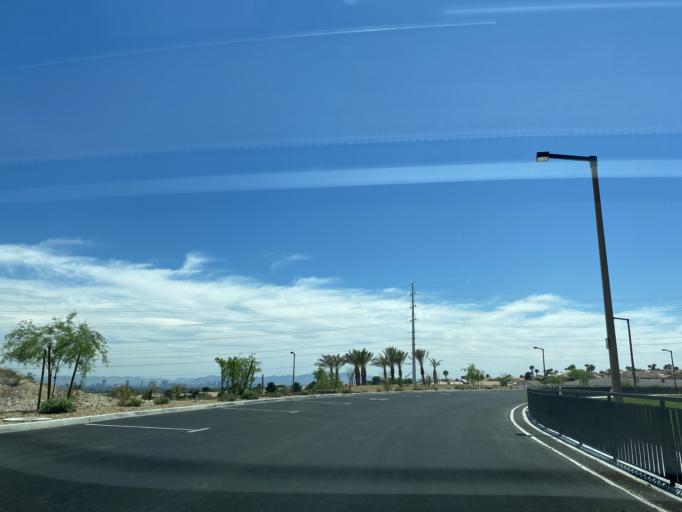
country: US
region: Nevada
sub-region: Clark County
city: Summerlin South
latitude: 36.2164
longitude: -115.3331
